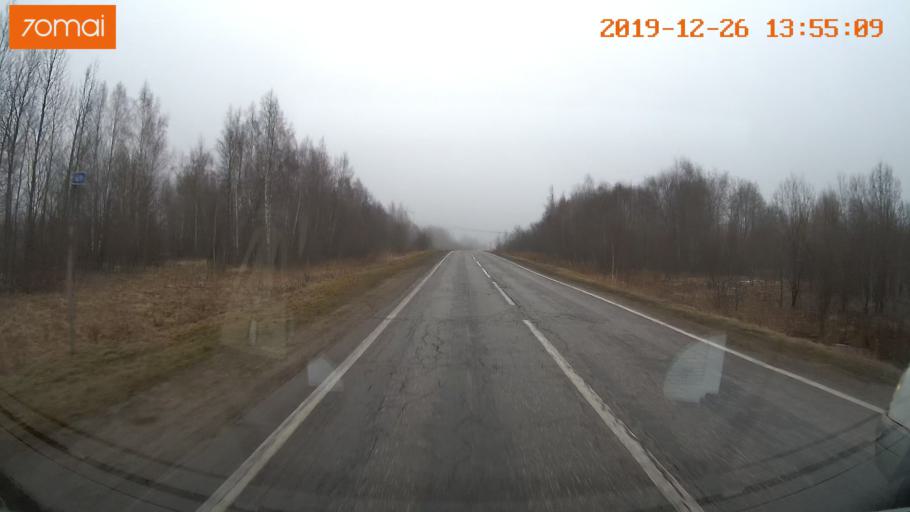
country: RU
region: Jaroslavl
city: Poshekhon'ye
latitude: 58.6066
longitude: 38.6437
